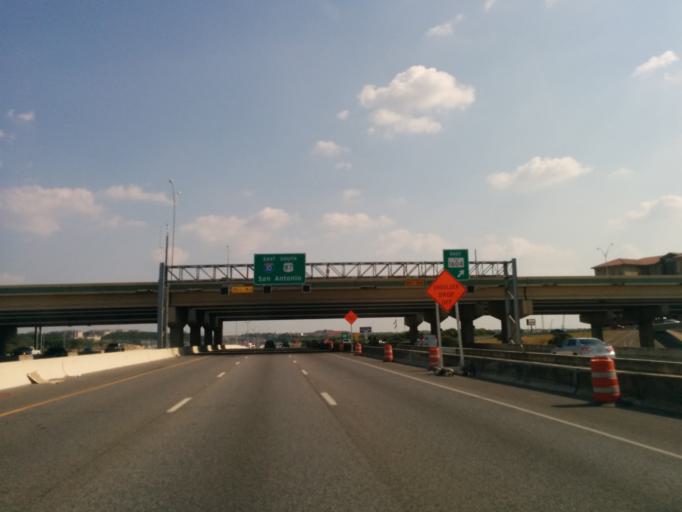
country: US
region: Texas
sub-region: Bexar County
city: Shavano Park
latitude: 29.5917
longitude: -98.5987
